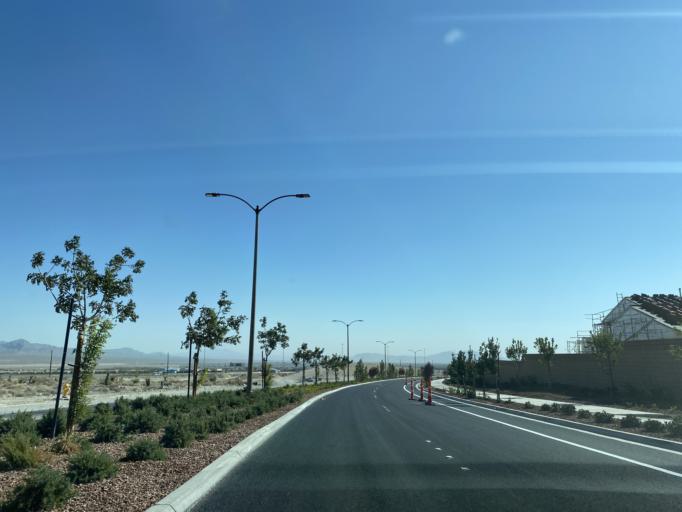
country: US
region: Nevada
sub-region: Clark County
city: Summerlin South
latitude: 36.3204
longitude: -115.3109
